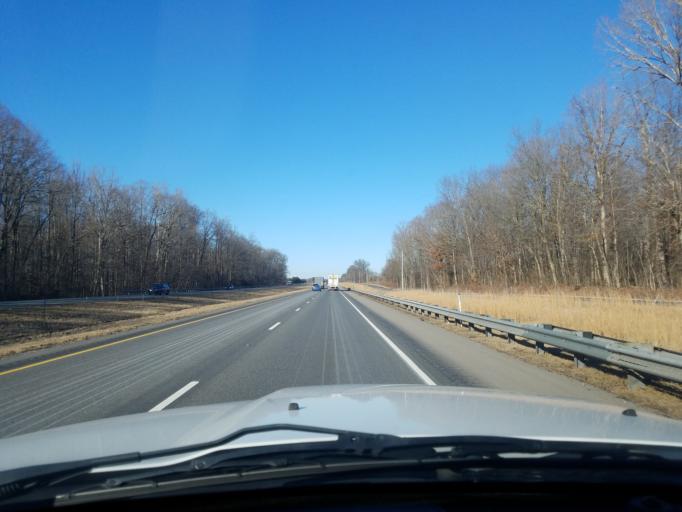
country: US
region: Indiana
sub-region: Jackson County
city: Crothersville
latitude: 38.8630
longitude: -85.8098
